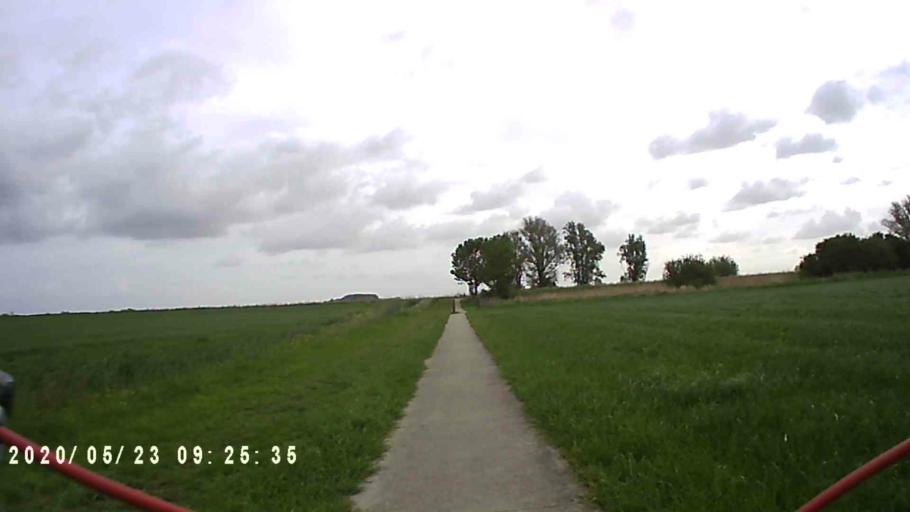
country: NL
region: Groningen
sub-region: Gemeente Bedum
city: Bedum
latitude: 53.2938
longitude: 6.6928
